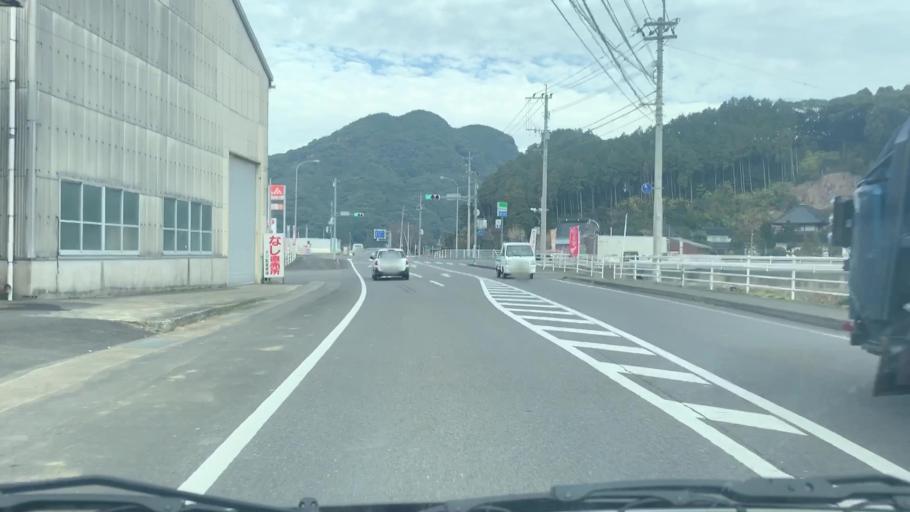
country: JP
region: Saga Prefecture
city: Imaricho-ko
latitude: 33.3009
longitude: 129.9694
